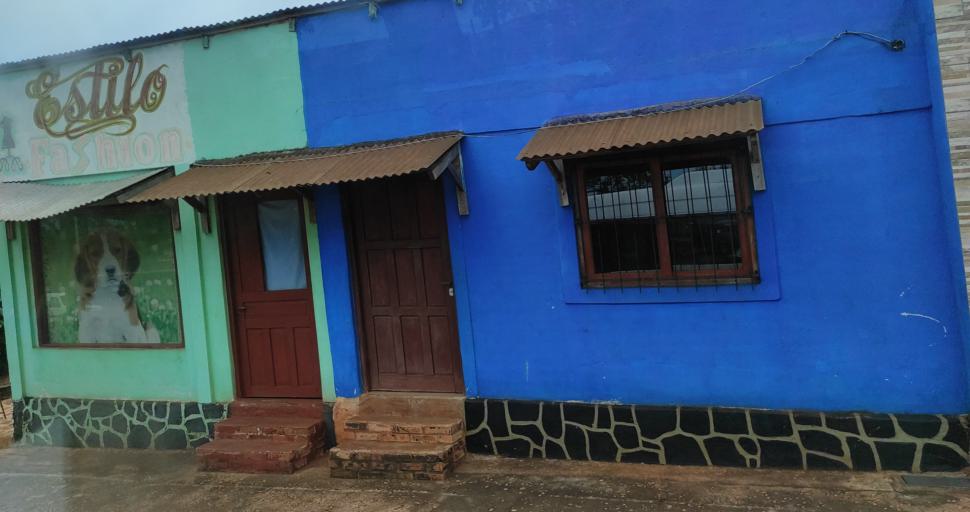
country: AR
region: Misiones
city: El Alcazar
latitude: -26.7093
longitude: -54.8164
